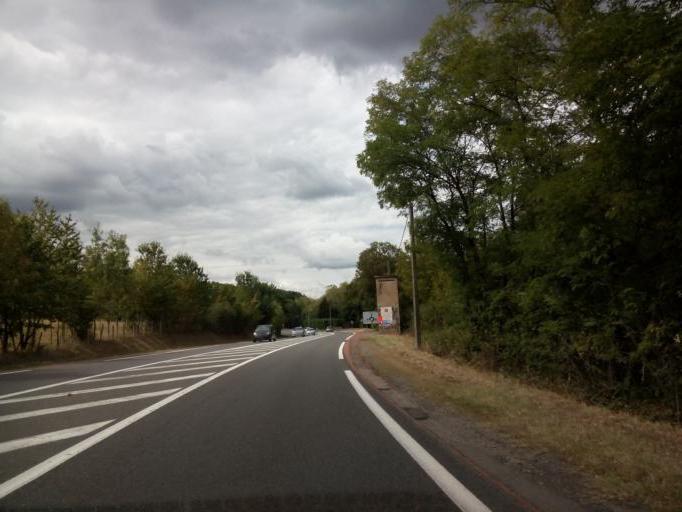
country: FR
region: Rhone-Alpes
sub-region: Departement du Rhone
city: Lissieu
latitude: 45.8449
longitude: 4.7288
